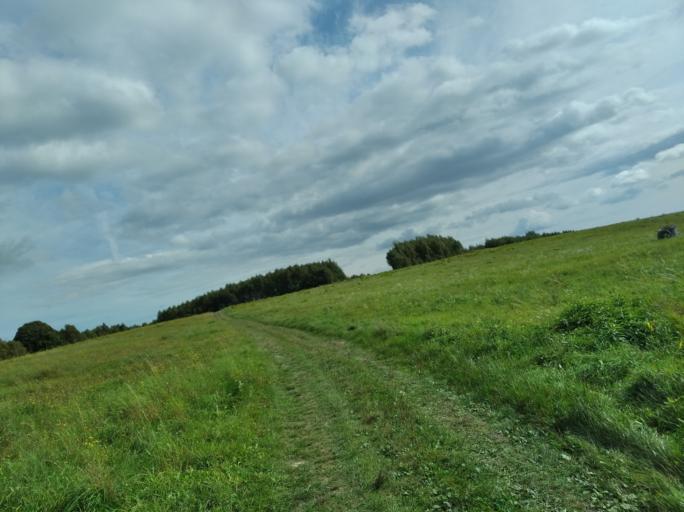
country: PL
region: Subcarpathian Voivodeship
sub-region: Powiat strzyzowski
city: Jawornik
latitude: 49.8342
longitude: 21.9058
